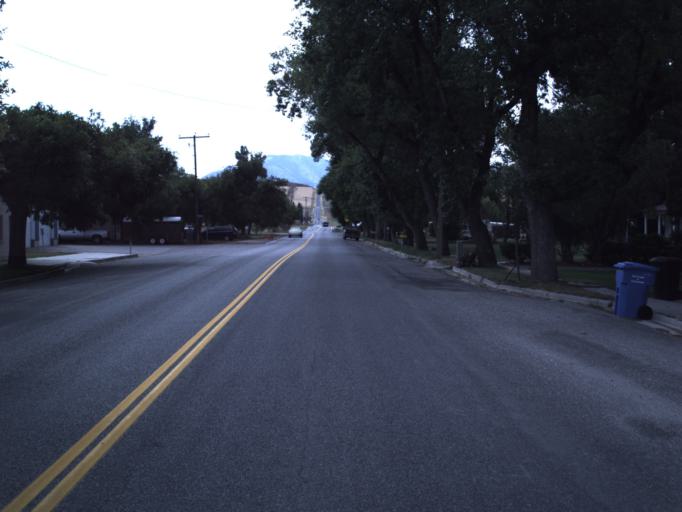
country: US
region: Utah
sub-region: Cache County
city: Lewiston
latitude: 41.9176
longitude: -111.9433
